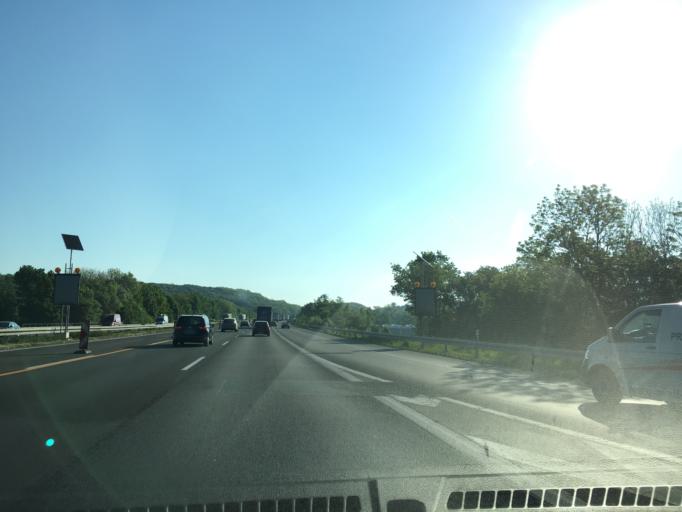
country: DE
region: North Rhine-Westphalia
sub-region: Regierungsbezirk Munster
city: Tecklenburg
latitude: 52.2019
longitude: 7.8108
